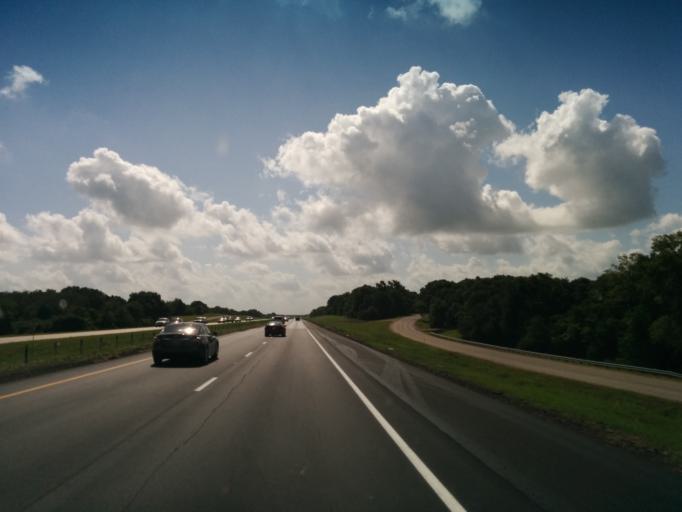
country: US
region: Texas
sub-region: Colorado County
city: Weimar
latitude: 29.6922
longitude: -96.7330
